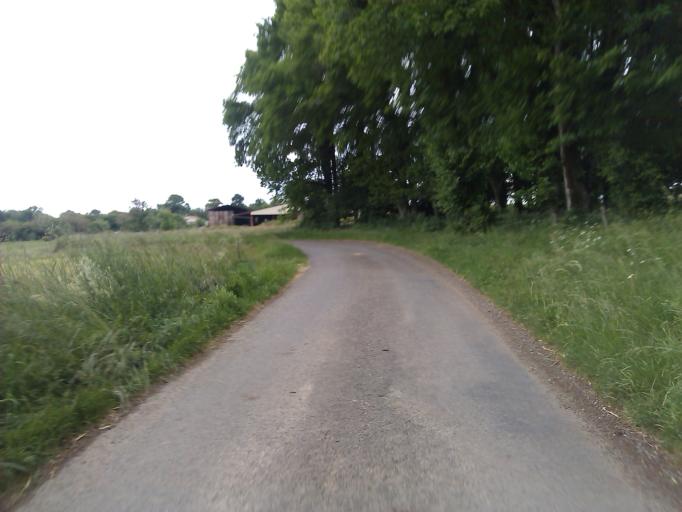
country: FR
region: Poitou-Charentes
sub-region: Departement de la Charente
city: Nanteuil-en-Vallee
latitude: 45.9683
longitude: 0.3151
